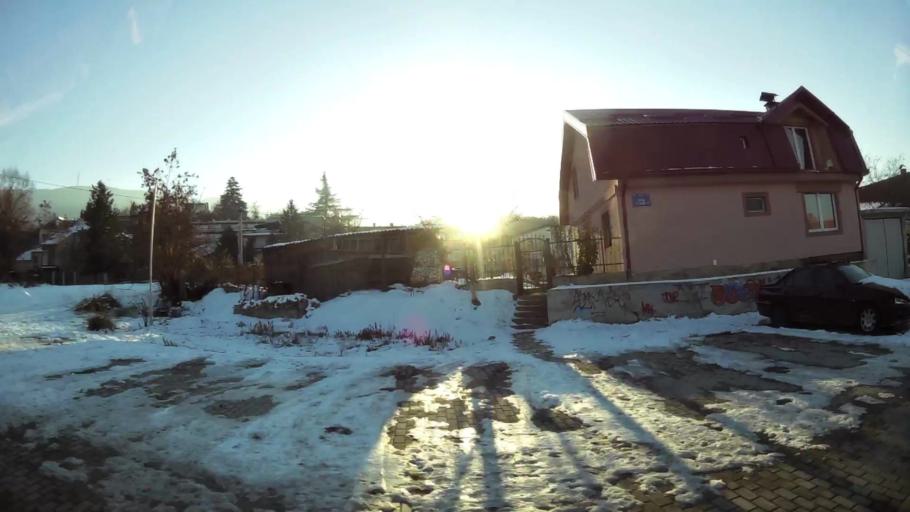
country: MK
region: Karpos
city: Skopje
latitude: 41.9961
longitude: 21.3950
